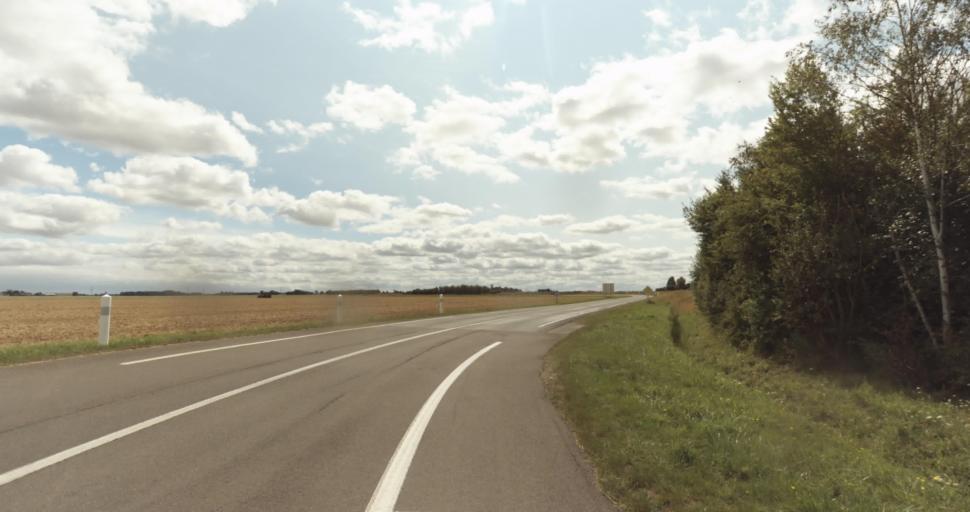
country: FR
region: Haute-Normandie
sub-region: Departement de l'Eure
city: Damville
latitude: 48.8873
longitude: 1.1769
